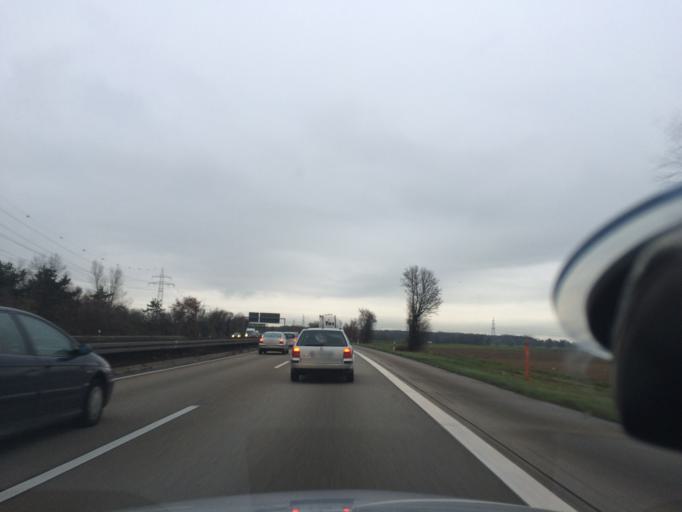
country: DE
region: Hesse
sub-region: Regierungsbezirk Darmstadt
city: Ginsheim-Gustavsburg
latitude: 49.9768
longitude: 8.3545
